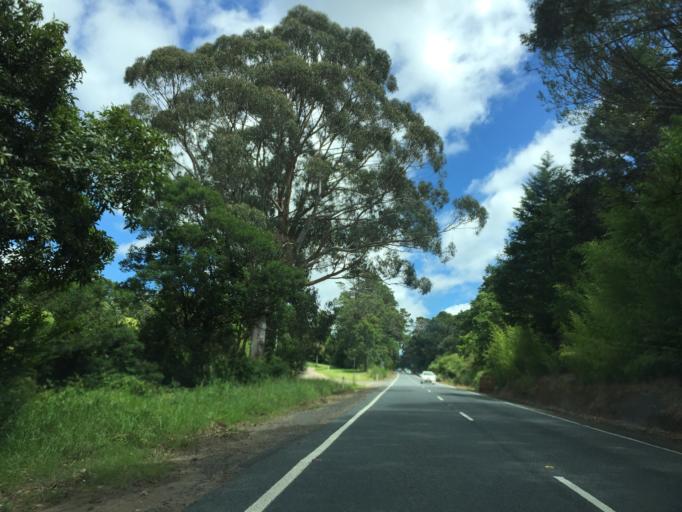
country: AU
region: New South Wales
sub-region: Blue Mountains Municipality
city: Hazelbrook
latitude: -33.5015
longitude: 150.5280
